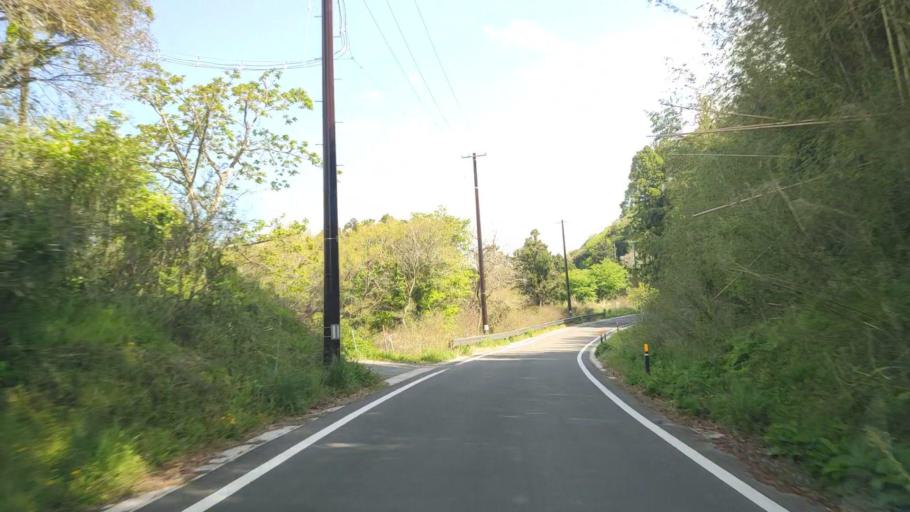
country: JP
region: Miyagi
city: Matsushima
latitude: 38.3371
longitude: 141.1600
